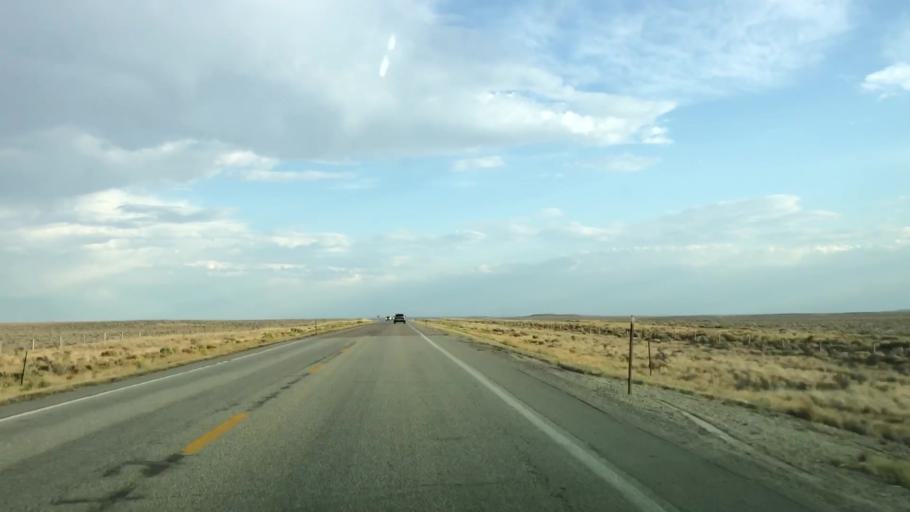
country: US
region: Wyoming
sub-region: Sublette County
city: Pinedale
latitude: 42.4113
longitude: -109.5528
